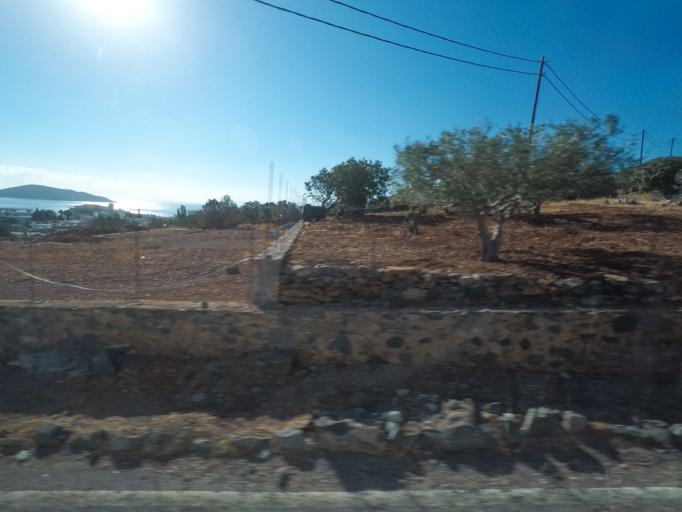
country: GR
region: Crete
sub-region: Nomos Lasithiou
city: Skhisma
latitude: 35.2460
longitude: 25.7265
